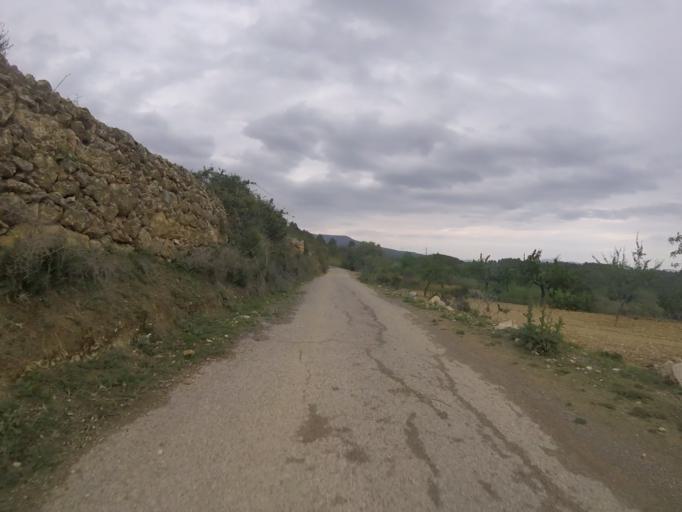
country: ES
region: Valencia
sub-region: Provincia de Castello
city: Sarratella
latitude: 40.2677
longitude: 0.0697
